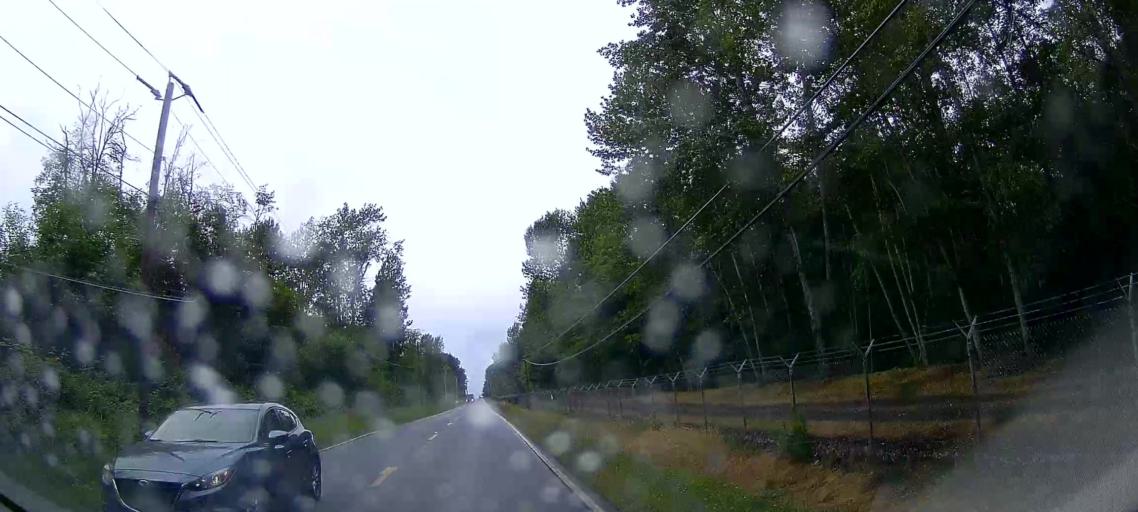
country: US
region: Washington
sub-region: Whatcom County
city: Ferndale
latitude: 48.8197
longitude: -122.6892
